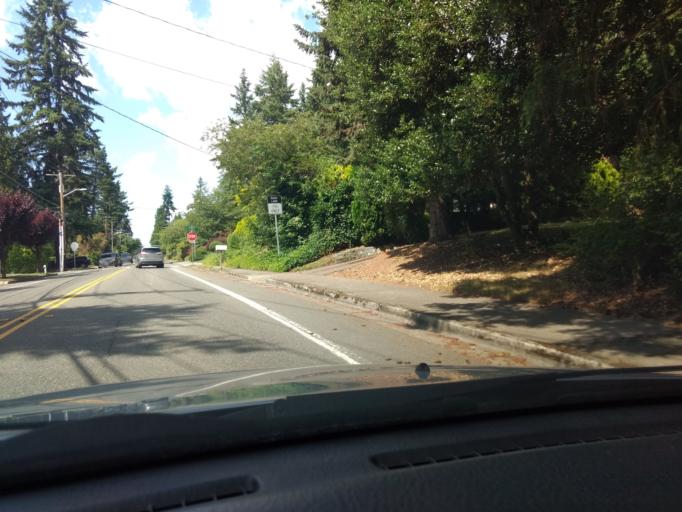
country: US
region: Washington
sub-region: King County
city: Bothell
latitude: 47.7653
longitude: -122.2062
